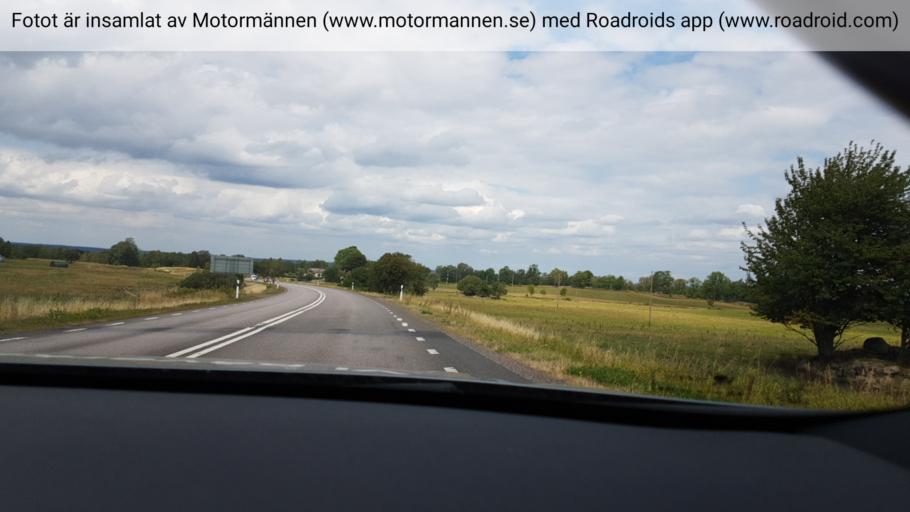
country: SE
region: Vaestra Goetaland
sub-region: Falkopings Kommun
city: Falkoeping
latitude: 58.2381
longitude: 13.5449
